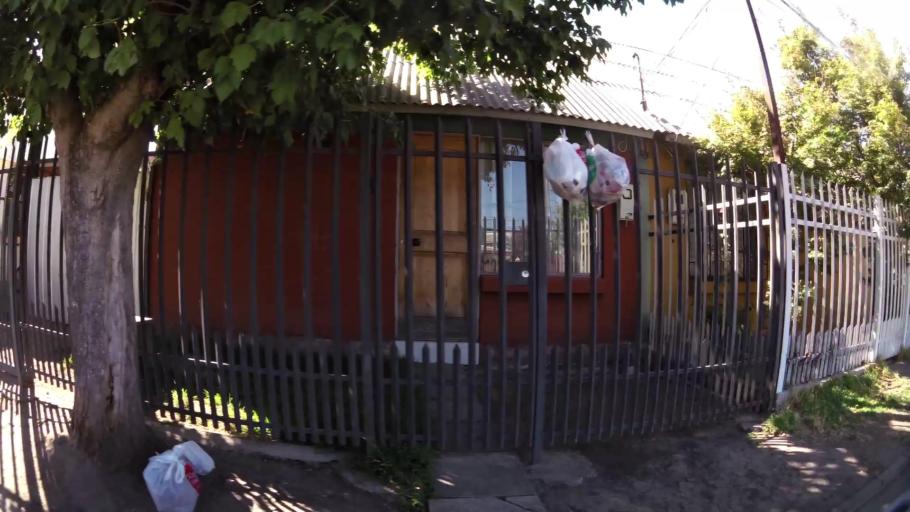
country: CL
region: Maule
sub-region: Provincia de Curico
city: Curico
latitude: -34.9777
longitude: -71.2651
